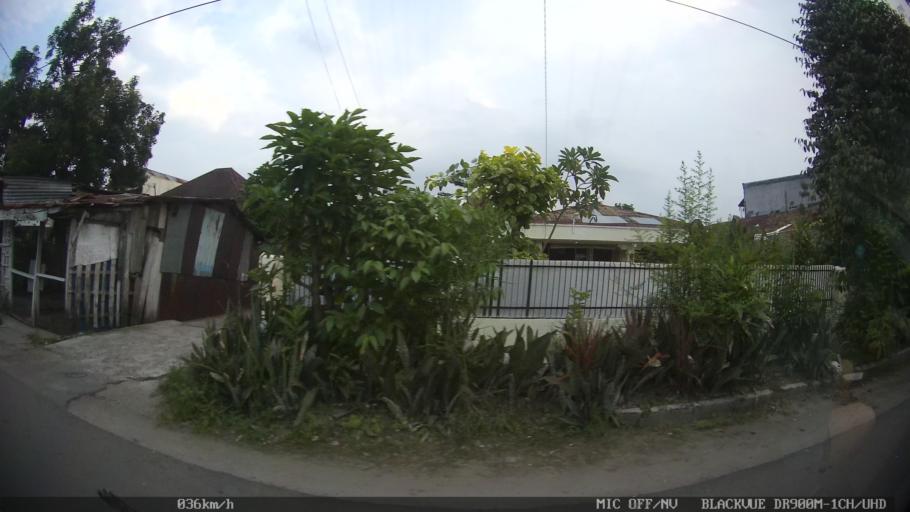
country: ID
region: North Sumatra
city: Medan
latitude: 3.6098
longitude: 98.6882
